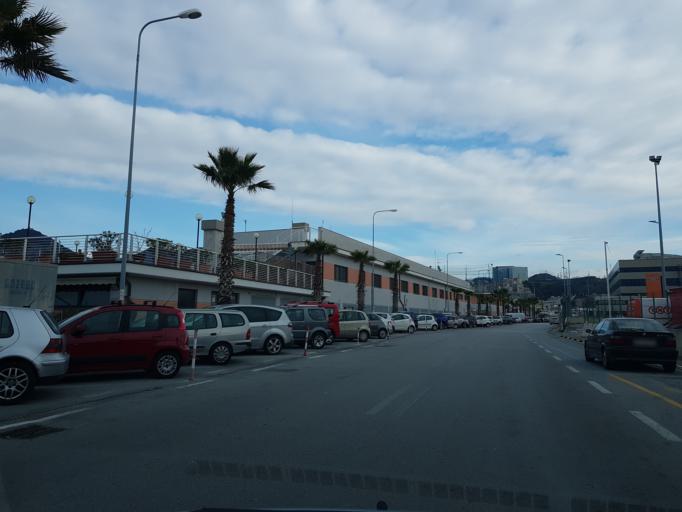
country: IT
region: Liguria
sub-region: Provincia di Genova
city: San Teodoro
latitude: 44.4159
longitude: 8.8443
